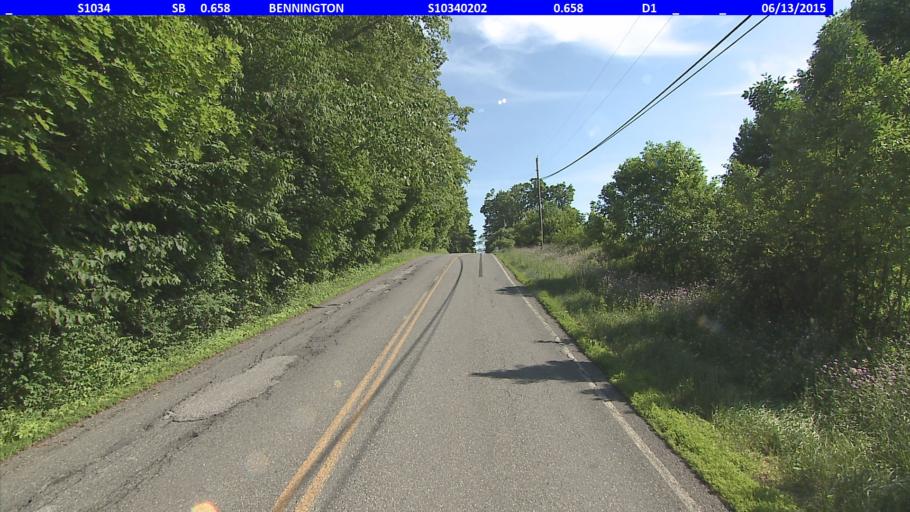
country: US
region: Vermont
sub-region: Bennington County
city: Bennington
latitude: 42.8615
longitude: -73.2061
